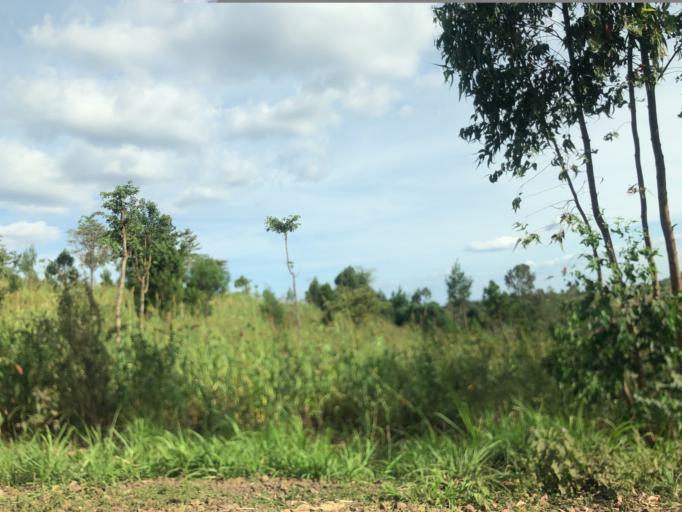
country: ET
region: Southern Nations, Nationalities, and People's Region
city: Konso
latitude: 5.2905
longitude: 37.3742
